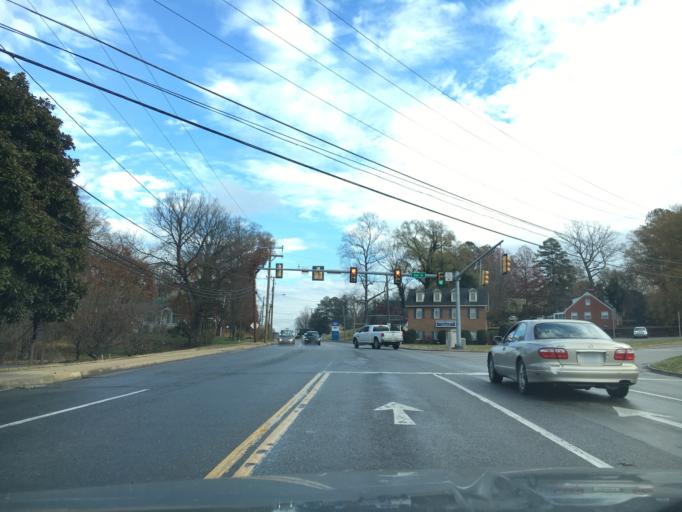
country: US
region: Virginia
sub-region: Prince Edward County
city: Farmville
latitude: 37.3037
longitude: -78.4042
